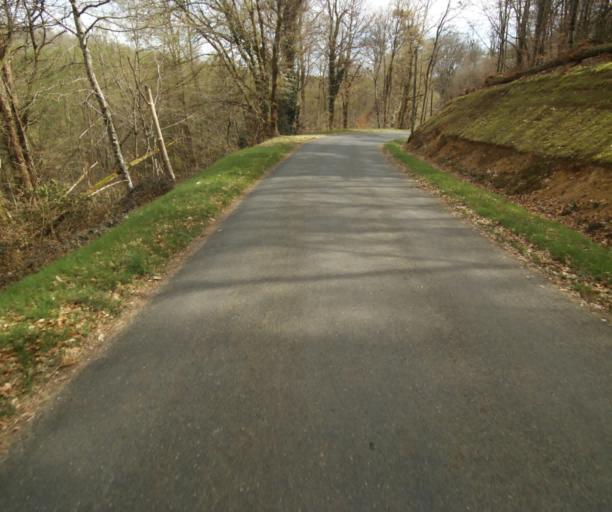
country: FR
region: Limousin
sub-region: Departement de la Correze
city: Naves
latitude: 45.3002
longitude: 1.7677
